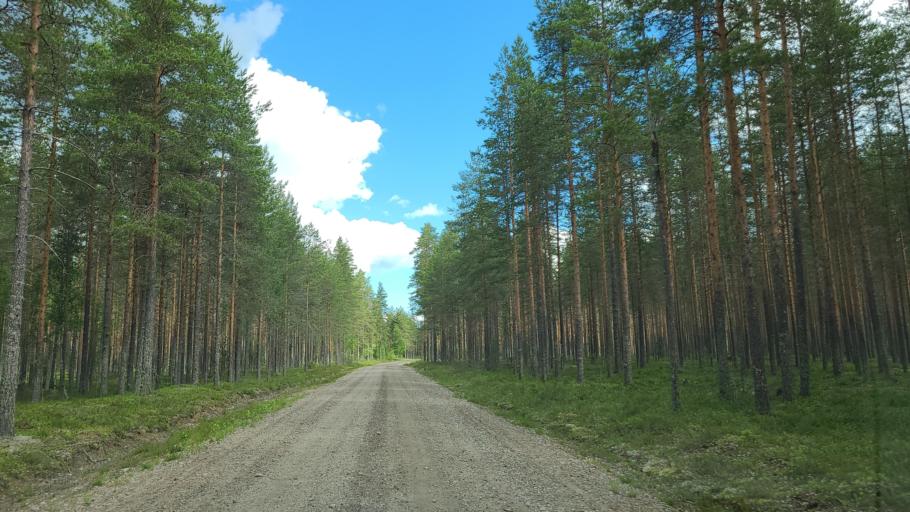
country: FI
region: Northern Savo
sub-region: Koillis-Savo
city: Kaavi
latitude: 63.0558
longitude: 28.8236
